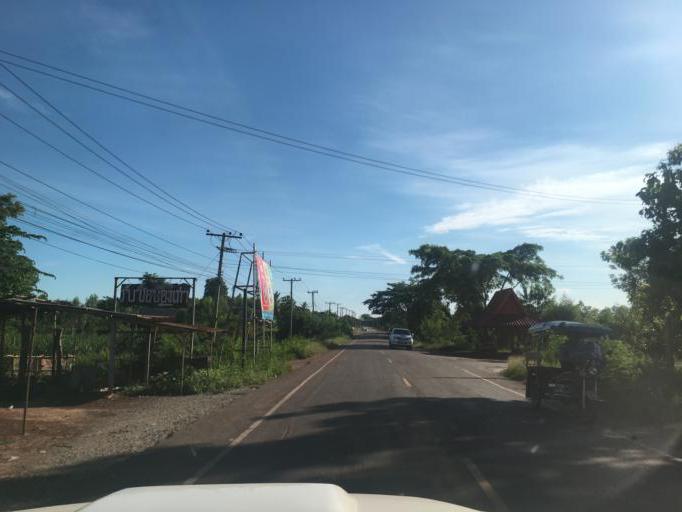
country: TH
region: Changwat Udon Thani
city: Kut Chap
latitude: 17.4677
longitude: 102.5883
